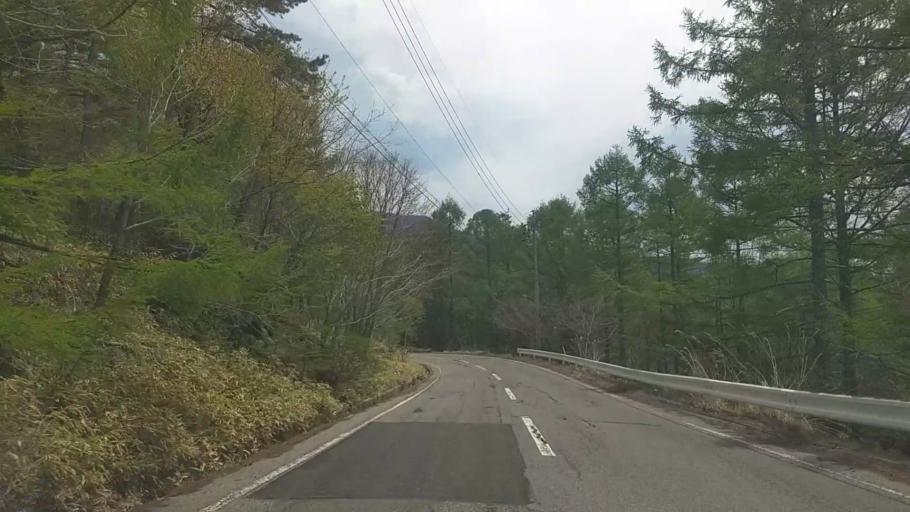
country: JP
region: Nagano
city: Chino
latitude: 36.0484
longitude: 138.3075
